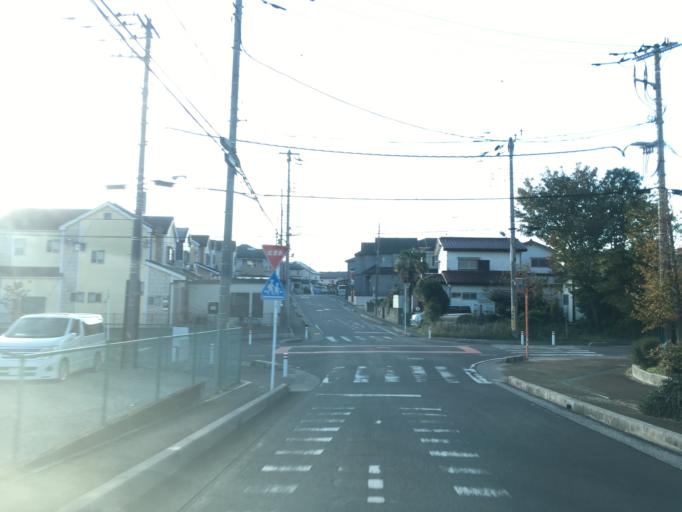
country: JP
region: Saitama
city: Tokorozawa
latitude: 35.7871
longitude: 139.4315
